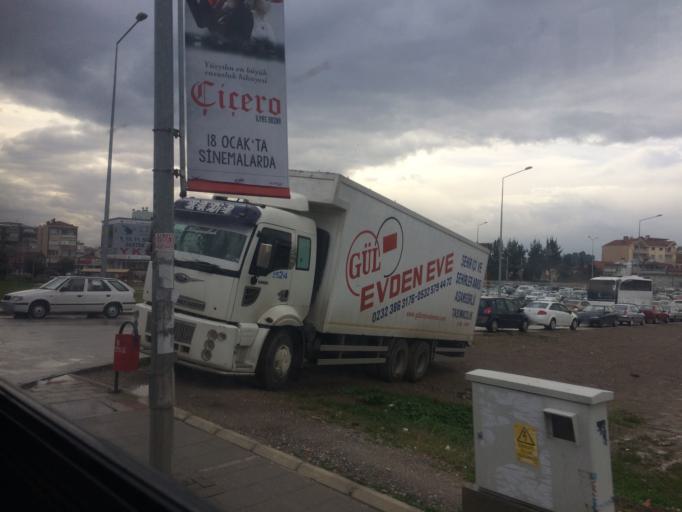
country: TR
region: Izmir
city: Karsiyaka
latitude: 38.4955
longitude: 27.0603
